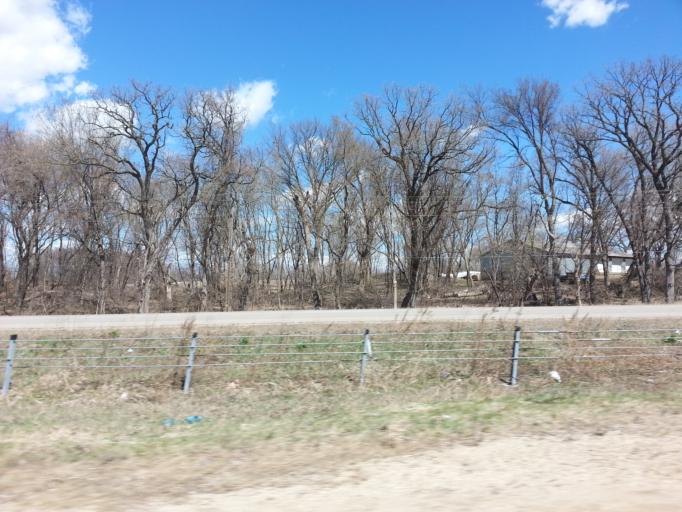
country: US
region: Minnesota
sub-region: Dakota County
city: Hastings
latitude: 44.7818
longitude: -92.8707
